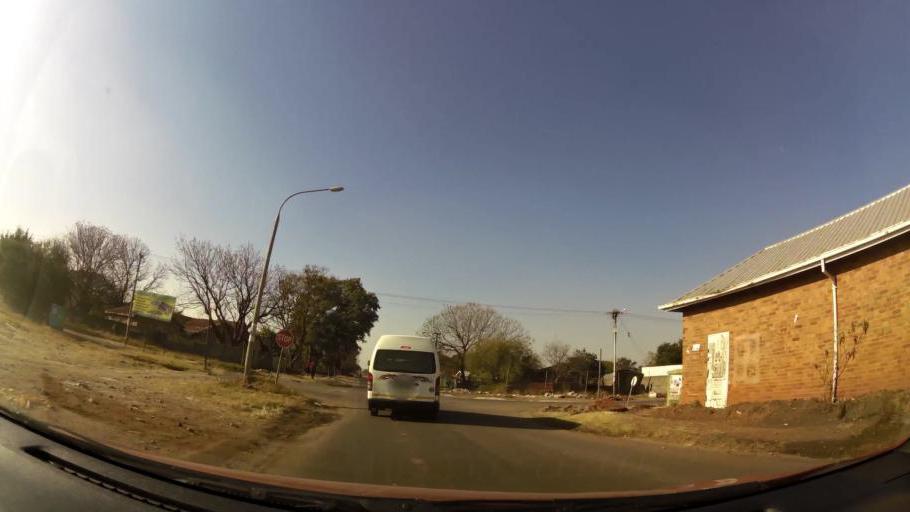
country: ZA
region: North-West
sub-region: Bojanala Platinum District Municipality
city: Rustenburg
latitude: -25.6570
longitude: 27.2279
